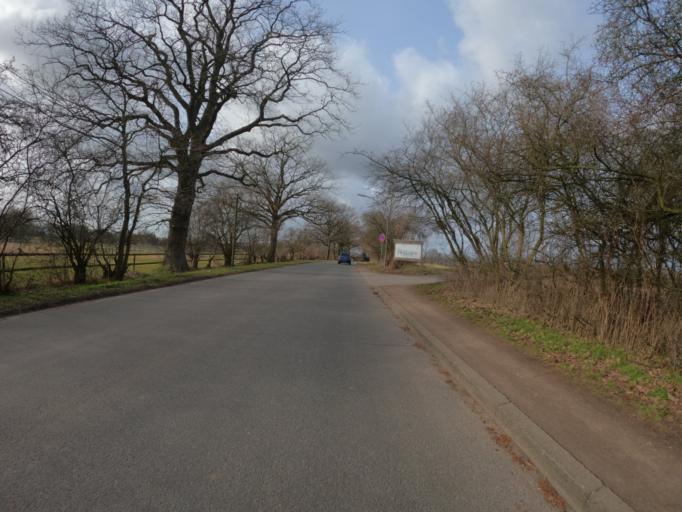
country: DE
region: Schleswig-Holstein
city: Halstenbek
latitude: 53.5778
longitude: 9.8396
